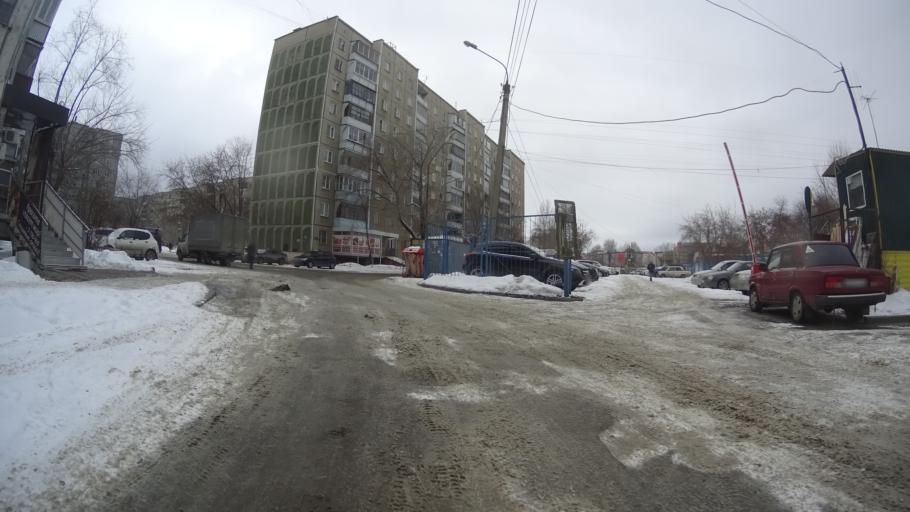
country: RU
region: Chelyabinsk
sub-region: Gorod Chelyabinsk
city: Chelyabinsk
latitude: 55.1772
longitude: 61.3410
